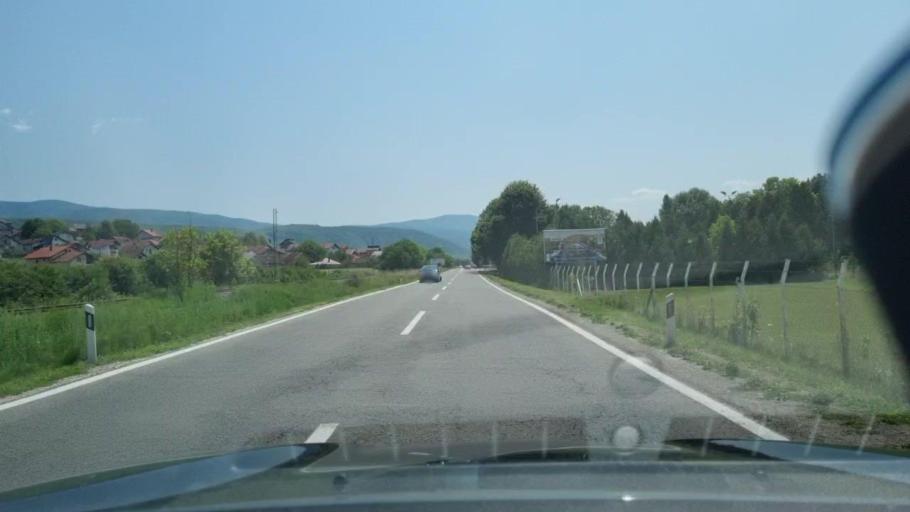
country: BA
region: Federation of Bosnia and Herzegovina
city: Bihac
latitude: 44.8030
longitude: 15.9042
